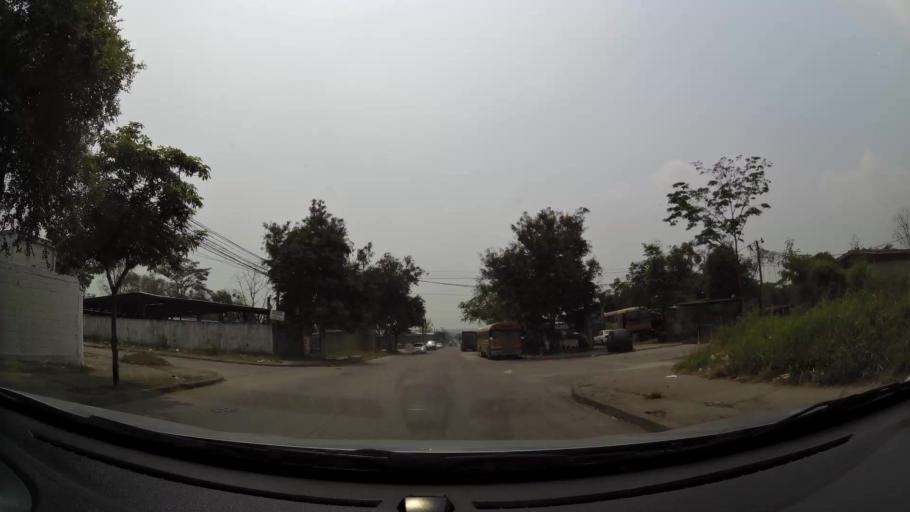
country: HN
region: Cortes
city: San Pedro Sula
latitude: 15.4838
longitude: -88.0278
